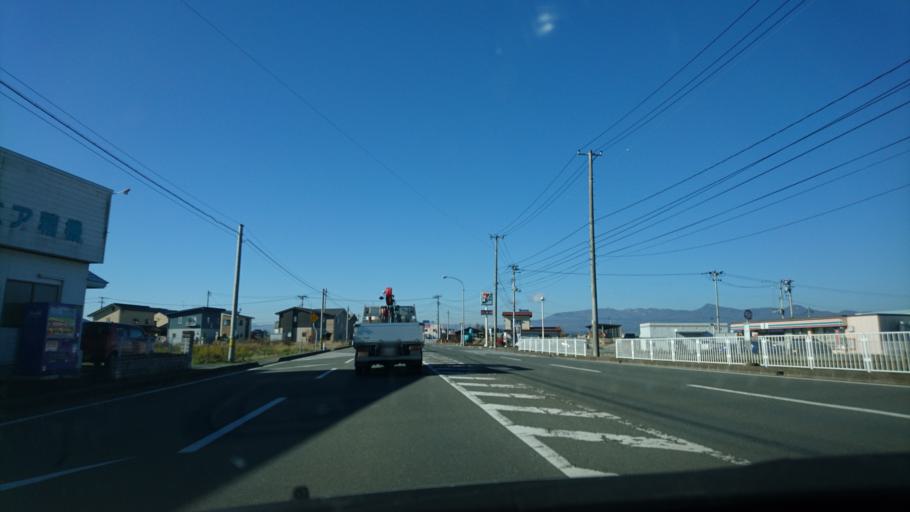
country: JP
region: Iwate
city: Mizusawa
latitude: 39.1446
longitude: 141.1151
